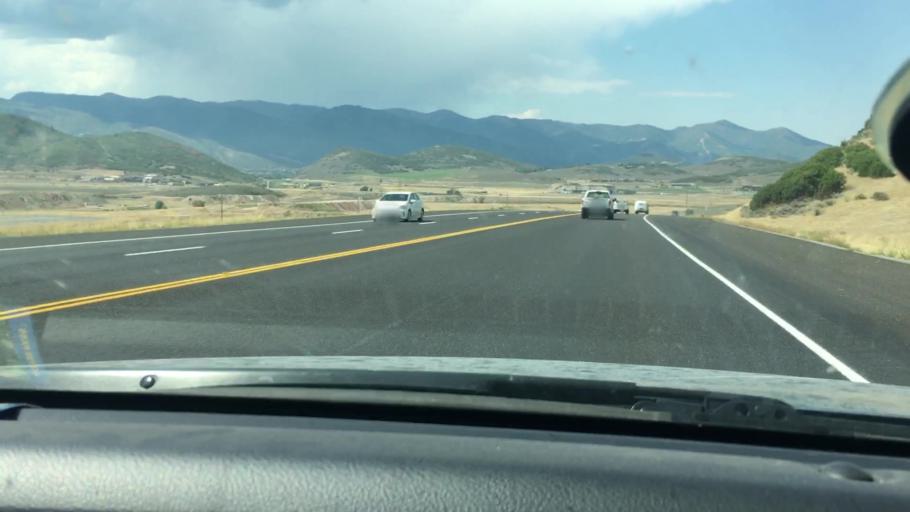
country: US
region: Utah
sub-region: Summit County
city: Park City
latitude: 40.6810
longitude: -111.4404
